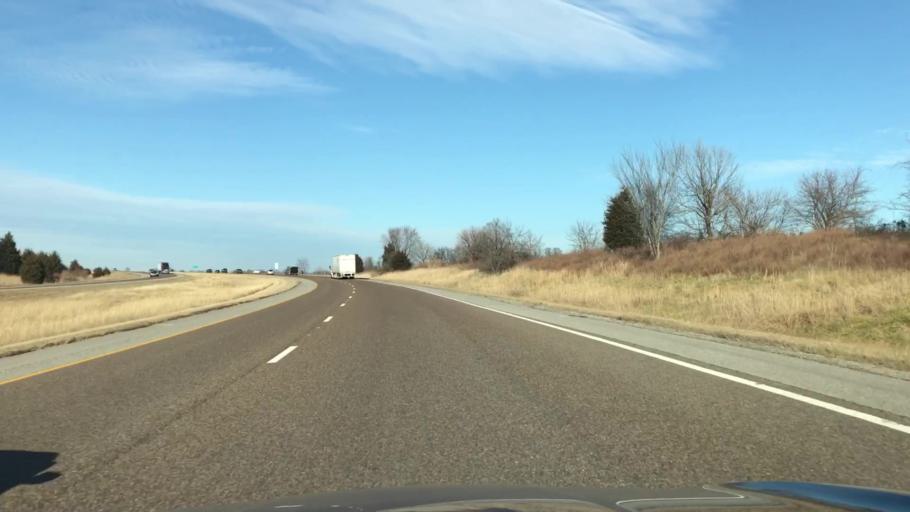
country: US
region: Illinois
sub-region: Macoupin County
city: Staunton
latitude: 38.9714
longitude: -89.7499
